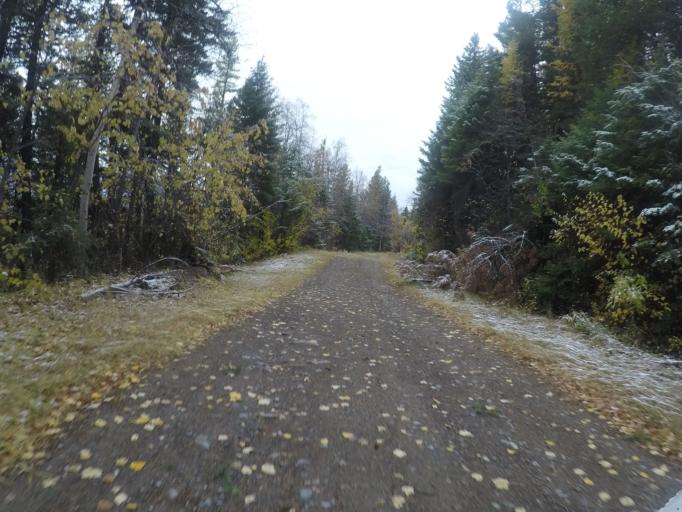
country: US
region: Montana
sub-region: Flathead County
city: Bigfork
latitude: 47.8914
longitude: -113.8749
